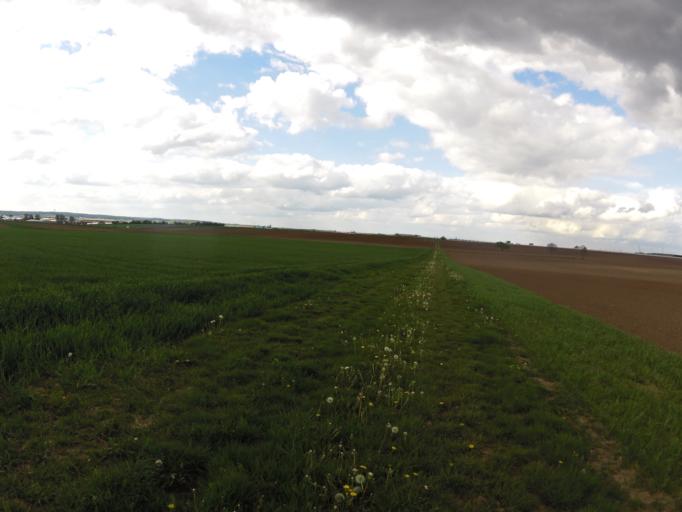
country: DE
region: Bavaria
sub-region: Regierungsbezirk Unterfranken
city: Oberpleichfeld
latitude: 49.8615
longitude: 10.0751
